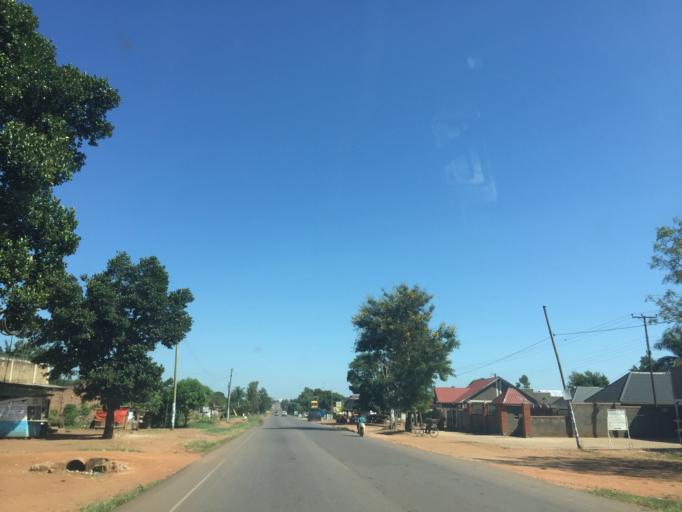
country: UG
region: Central Region
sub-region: Luwero District
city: Luwero
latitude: 0.8150
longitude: 32.5043
